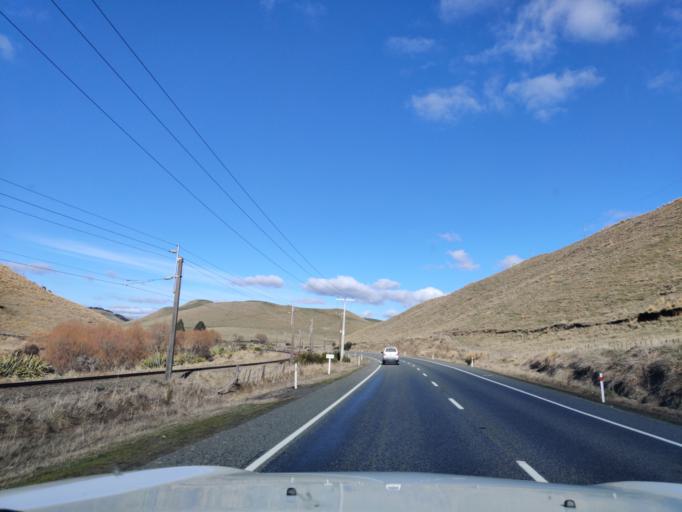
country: NZ
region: Manawatu-Wanganui
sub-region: Ruapehu District
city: Waiouru
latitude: -39.5033
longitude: 175.6739
